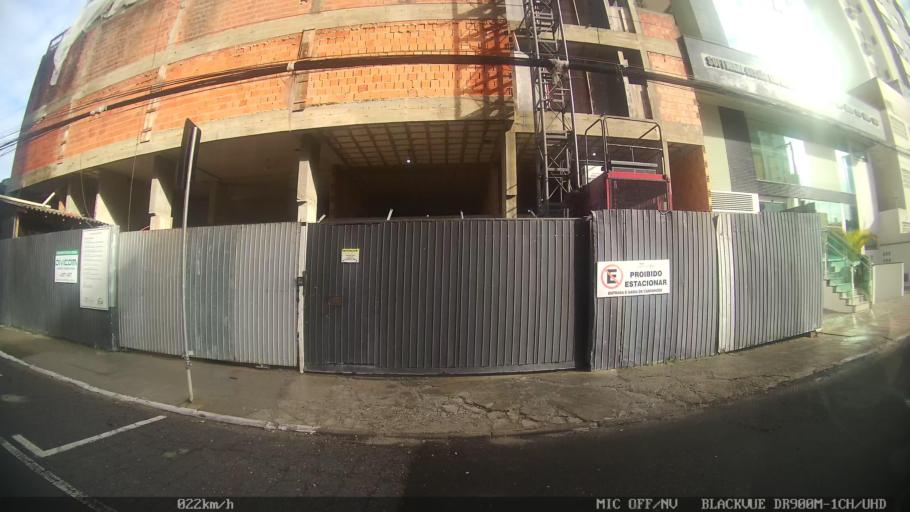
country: BR
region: Santa Catarina
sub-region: Sao Jose
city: Campinas
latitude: -27.5976
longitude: -48.6162
